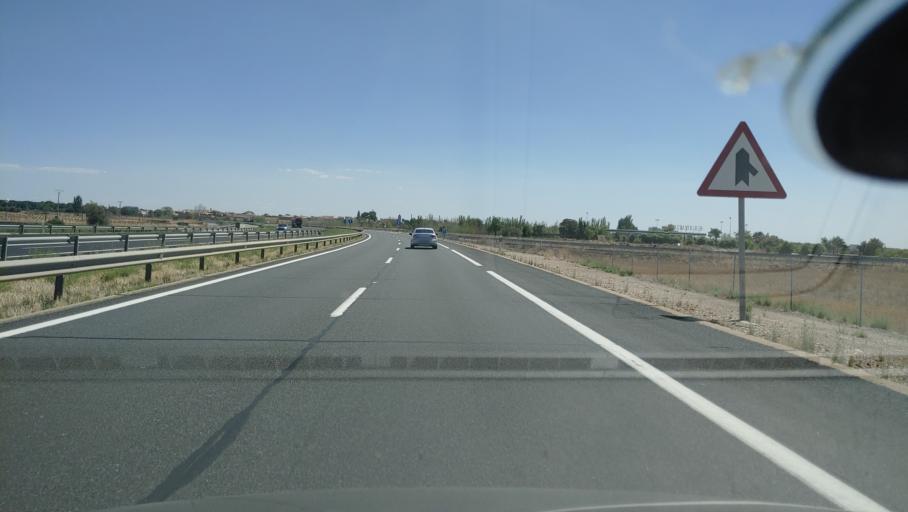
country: ES
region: Castille-La Mancha
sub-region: Provincia de Ciudad Real
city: Villarta de San Juan
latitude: 39.2502
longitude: -3.4314
